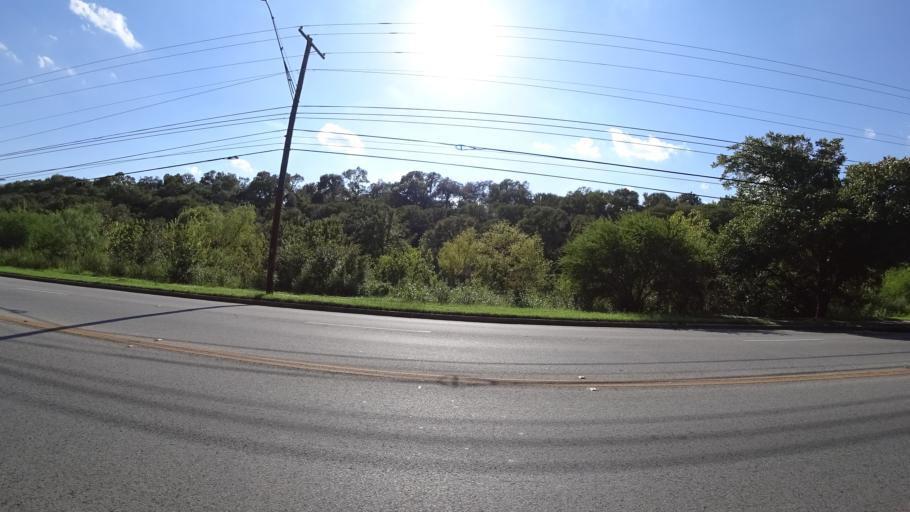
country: US
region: Texas
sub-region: Travis County
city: Austin
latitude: 30.2955
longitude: -97.7483
